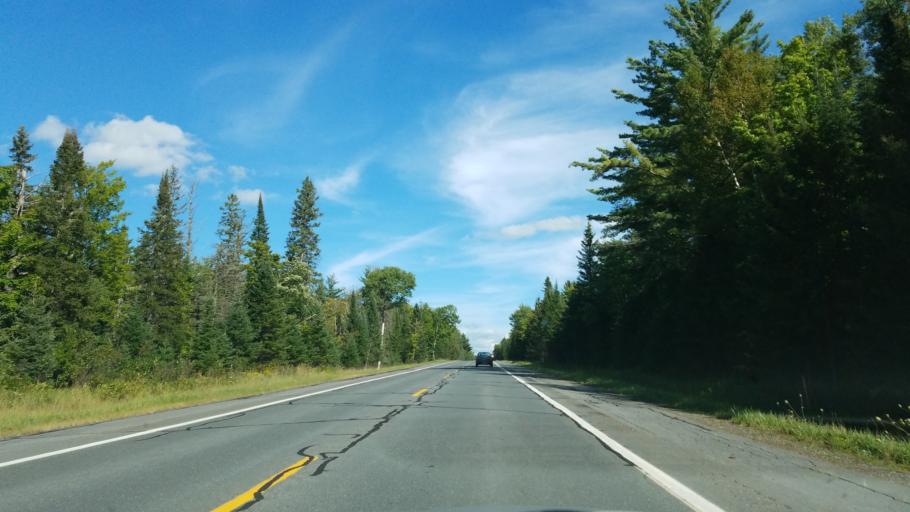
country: US
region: Michigan
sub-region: Baraga County
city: L'Anse
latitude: 46.5788
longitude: -88.4105
